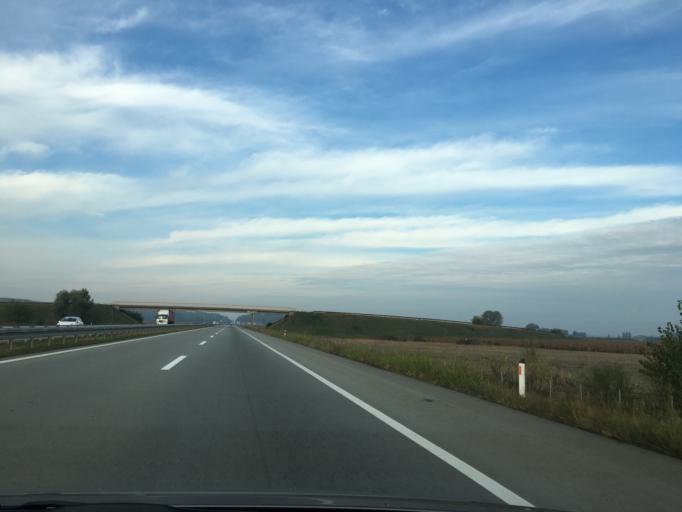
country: RS
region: Autonomna Pokrajina Vojvodina
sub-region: Juznobacki Okrug
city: Petrovaradin
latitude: 45.2719
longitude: 19.9414
